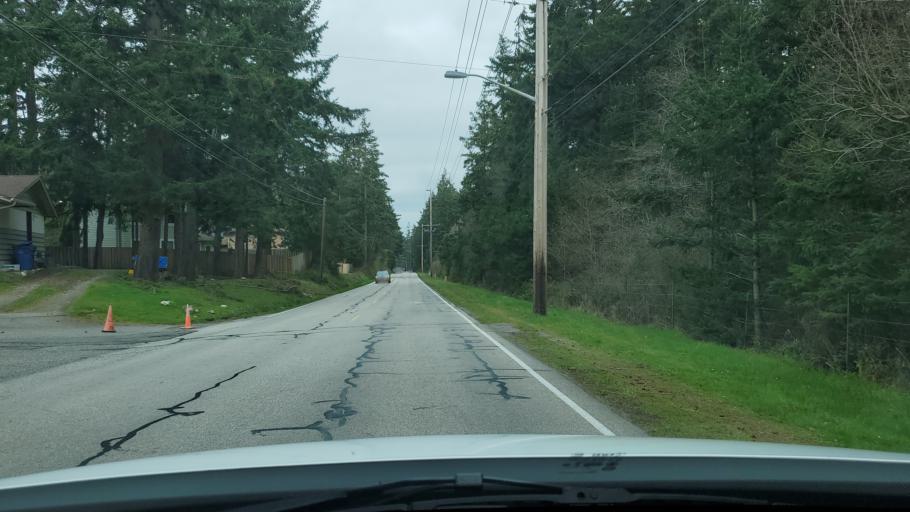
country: US
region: Washington
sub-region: Island County
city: Oak Harbor
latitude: 48.3043
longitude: -122.6330
